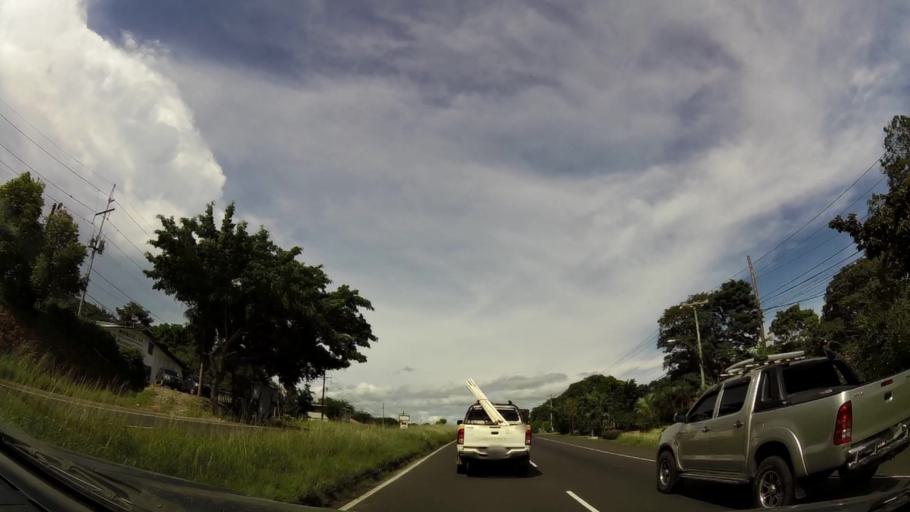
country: PA
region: Panama
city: Capira
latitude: 8.7348
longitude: -79.8833
